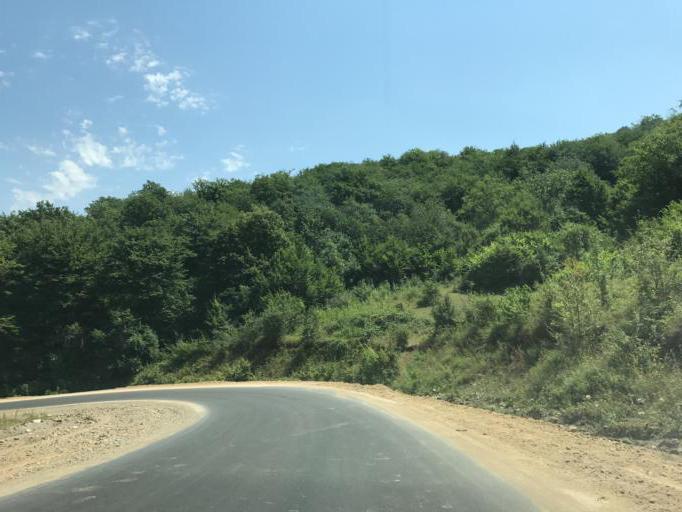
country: AZ
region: Tartar Rayon
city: Martakert
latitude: 40.1238
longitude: 46.6264
